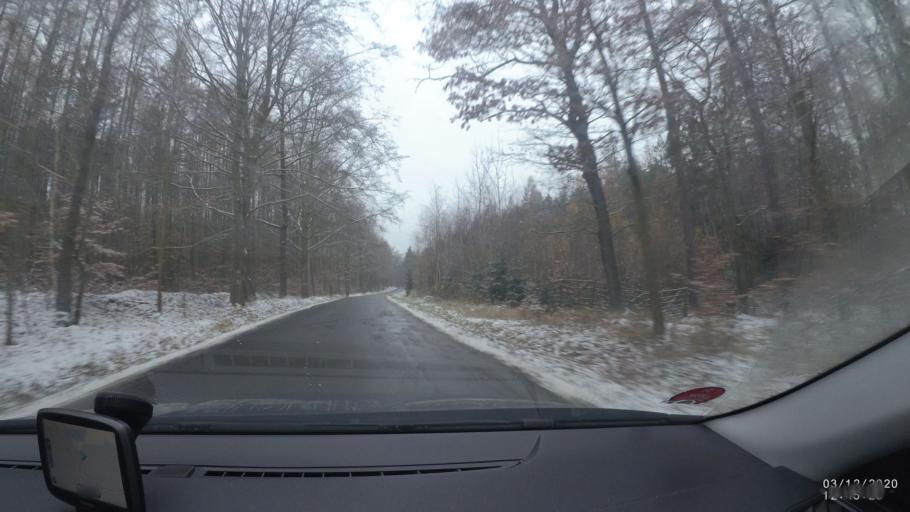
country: CZ
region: Central Bohemia
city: Revnicov
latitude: 50.1706
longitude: 13.8446
